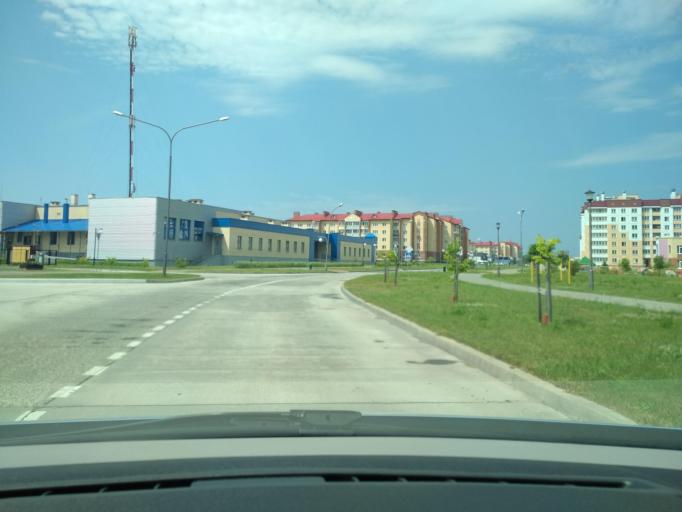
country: BY
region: Grodnenskaya
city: Astravyets
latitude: 54.6053
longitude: 25.9731
